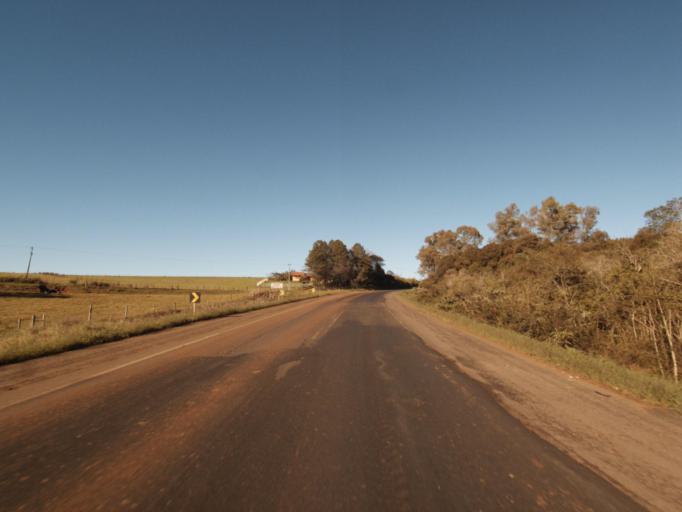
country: BR
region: Rio Grande do Sul
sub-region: Frederico Westphalen
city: Frederico Westphalen
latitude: -26.9124
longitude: -53.1878
